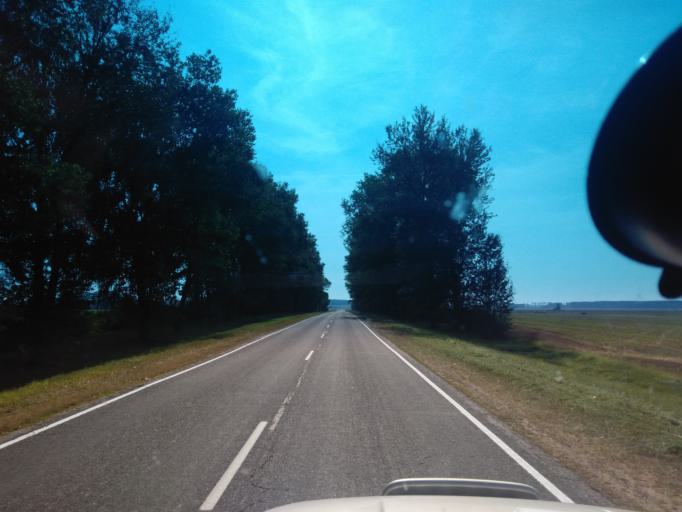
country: BY
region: Minsk
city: Uzda
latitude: 53.4047
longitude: 27.2240
